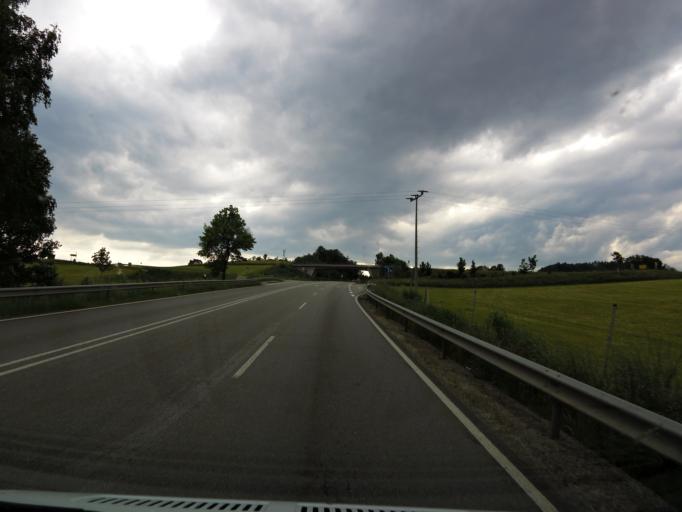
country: DE
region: Bavaria
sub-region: Lower Bavaria
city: Witzmannsberg
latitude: 48.6889
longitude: 13.4277
